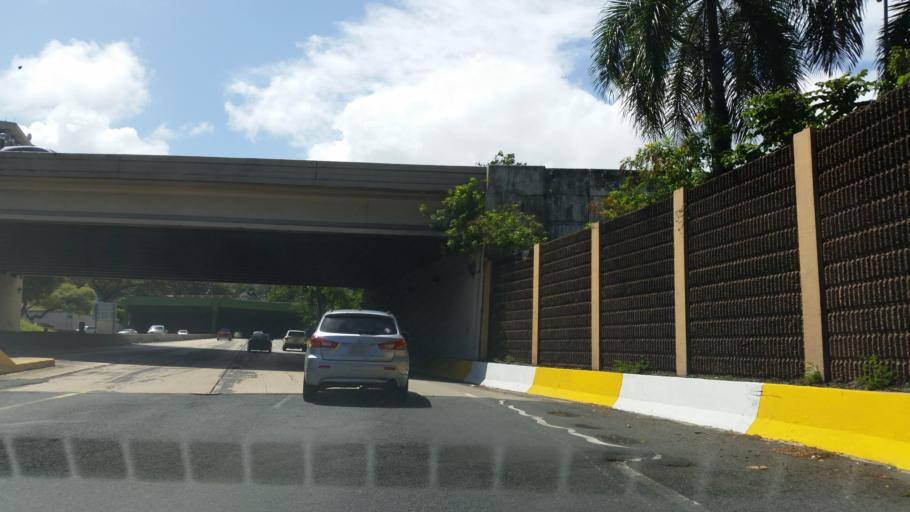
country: PR
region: San Juan
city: San Juan
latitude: 18.4515
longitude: -66.0684
